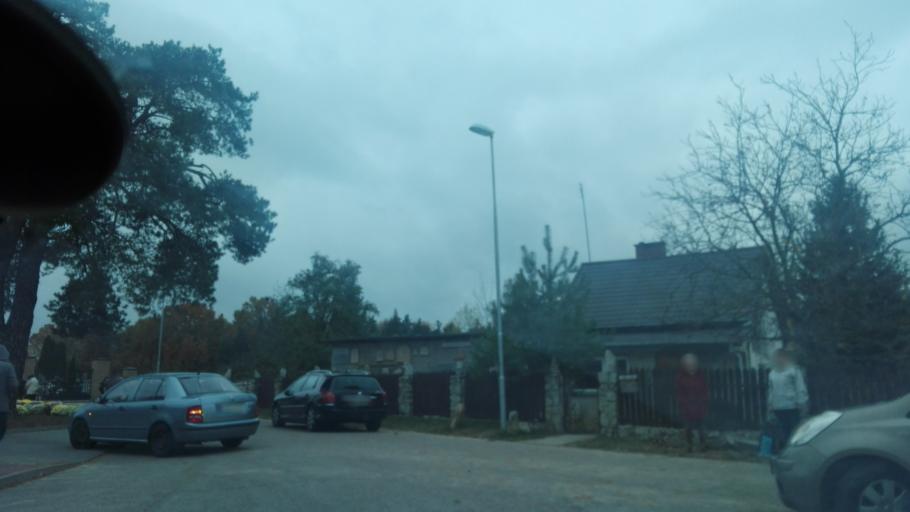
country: PL
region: Lublin Voivodeship
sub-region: Powiat pulawski
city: Pulawy
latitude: 51.4105
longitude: 21.9240
